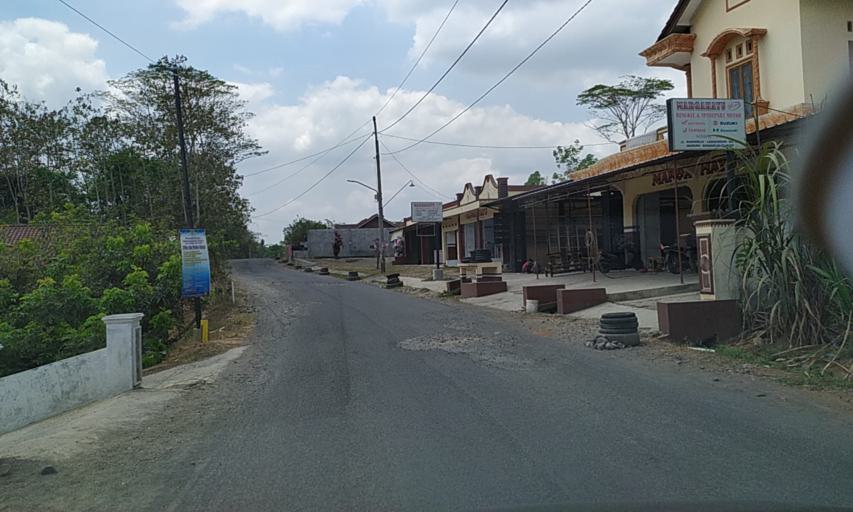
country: ID
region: Central Java
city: Karanganyar
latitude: -7.3346
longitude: 108.6305
